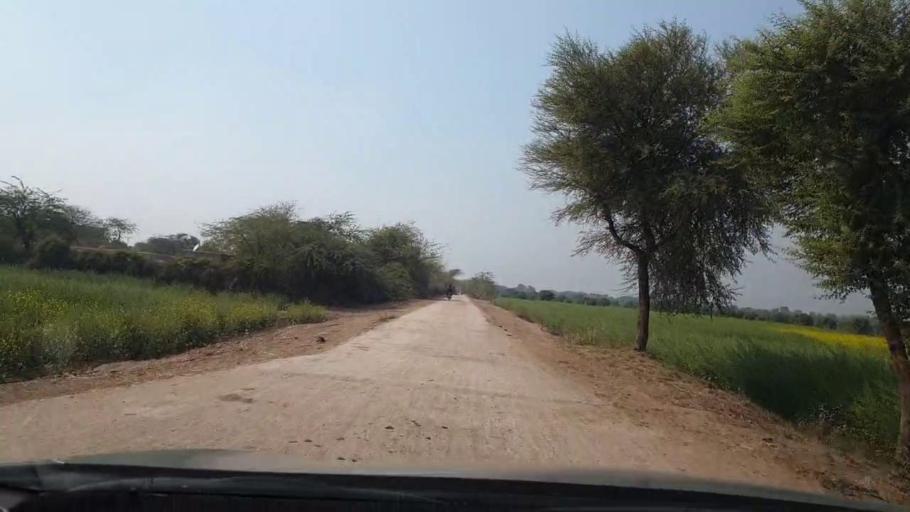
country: PK
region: Sindh
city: Tando Allahyar
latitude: 25.5058
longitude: 68.7955
